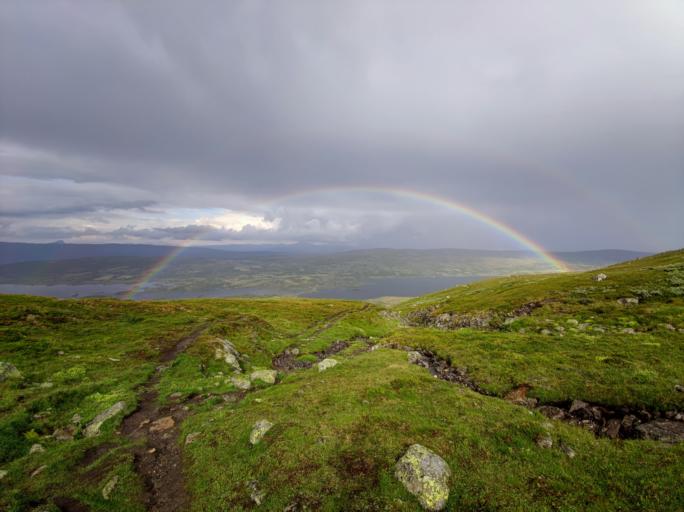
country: NO
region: Oppland
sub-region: Vang
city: Vang
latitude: 61.0654
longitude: 8.7018
